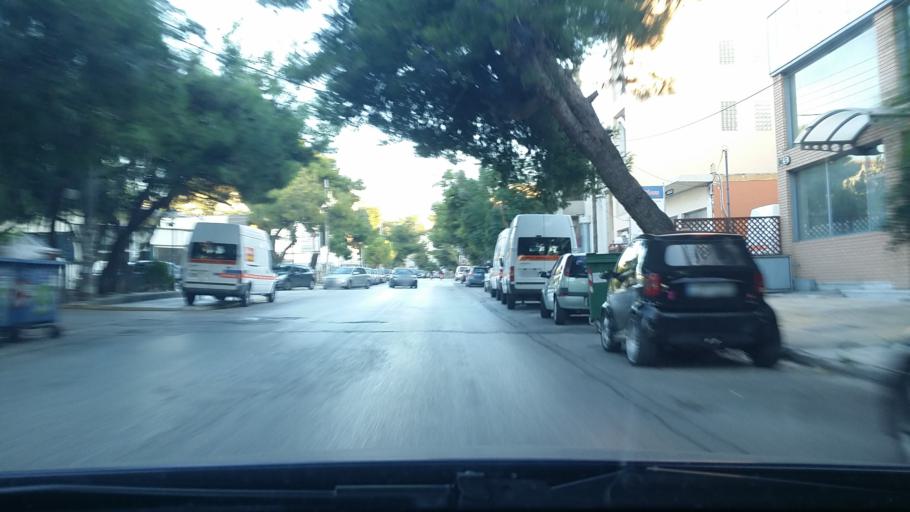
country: GR
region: Attica
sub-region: Nomarchia Athinas
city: Irakleio
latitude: 38.0488
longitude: 23.7542
